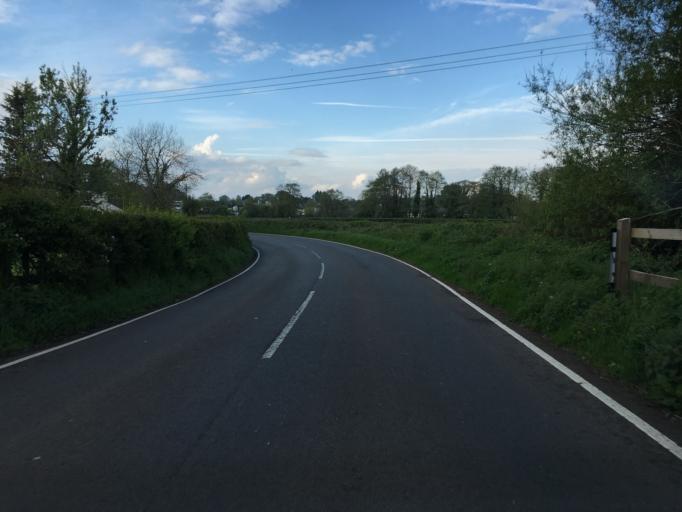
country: GB
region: Wales
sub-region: Monmouthshire
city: Llanarth
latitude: 51.7608
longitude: -2.8499
